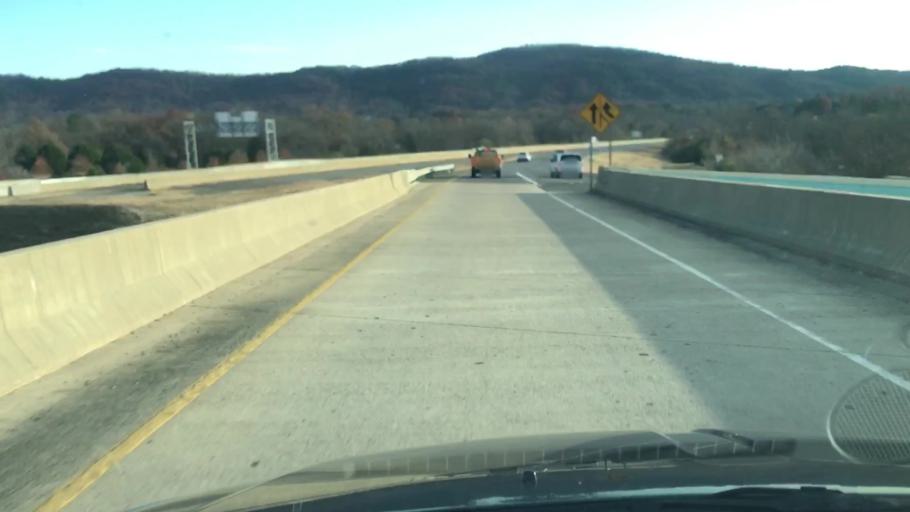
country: US
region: Arkansas
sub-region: Garland County
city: Hot Springs National Park
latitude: 34.5029
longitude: -92.9759
